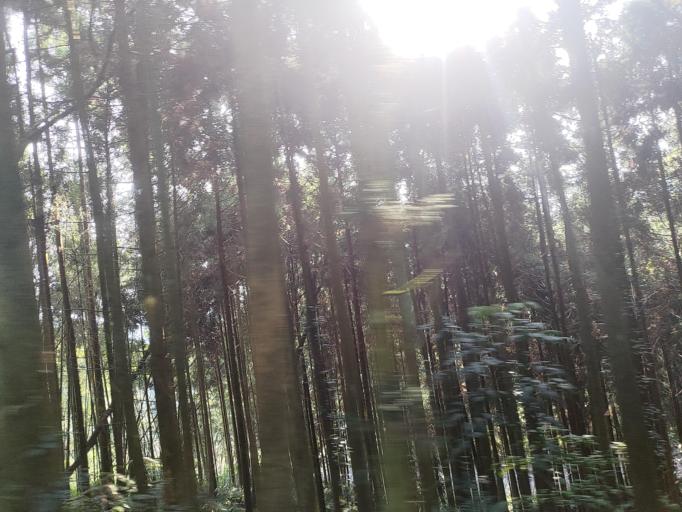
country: TW
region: Taiwan
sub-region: Hsinchu
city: Hsinchu
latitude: 24.6281
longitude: 121.0864
